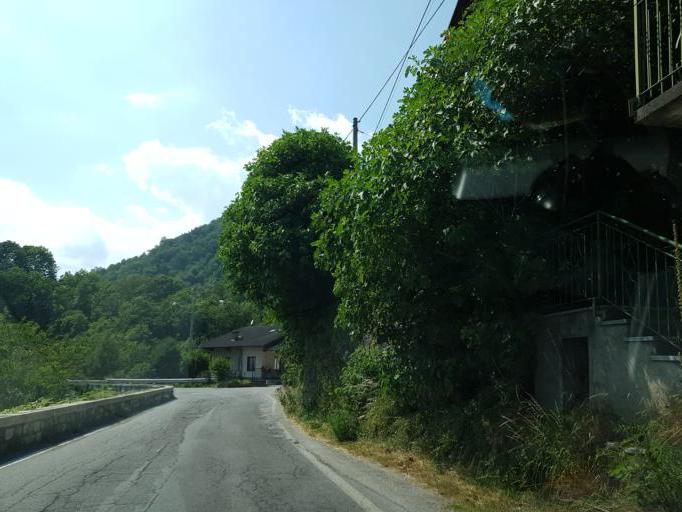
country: IT
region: Piedmont
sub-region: Provincia di Cuneo
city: San Damiano Macra
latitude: 44.4897
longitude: 7.2538
